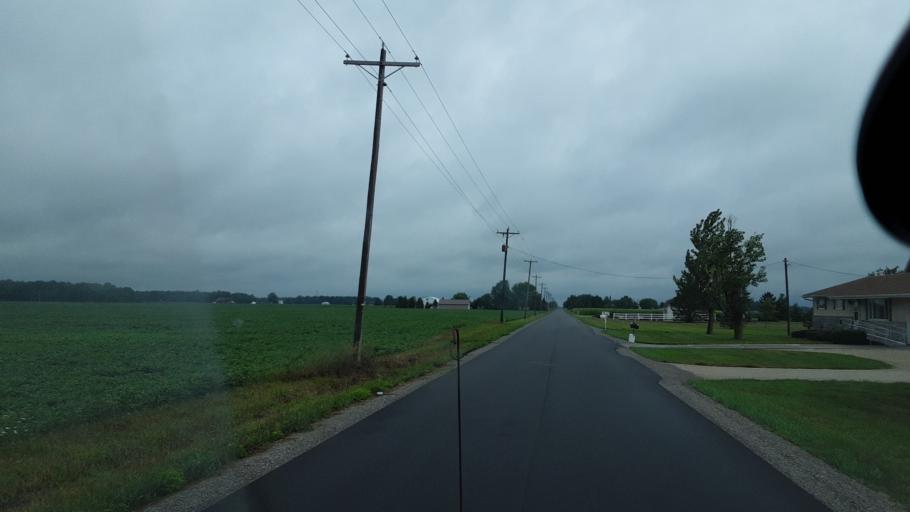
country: US
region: Indiana
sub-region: Adams County
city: Decatur
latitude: 40.8437
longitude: -84.8427
